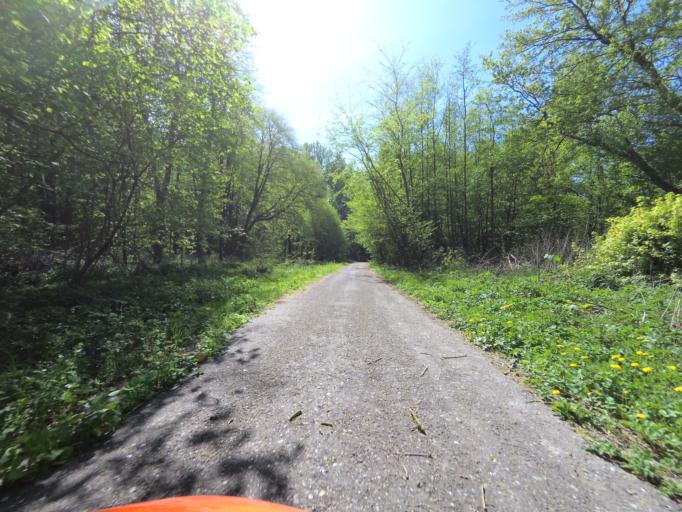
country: NL
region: Gelderland
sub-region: Gemeente Harderwijk
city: Harderwijk
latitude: 52.3995
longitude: 5.6271
